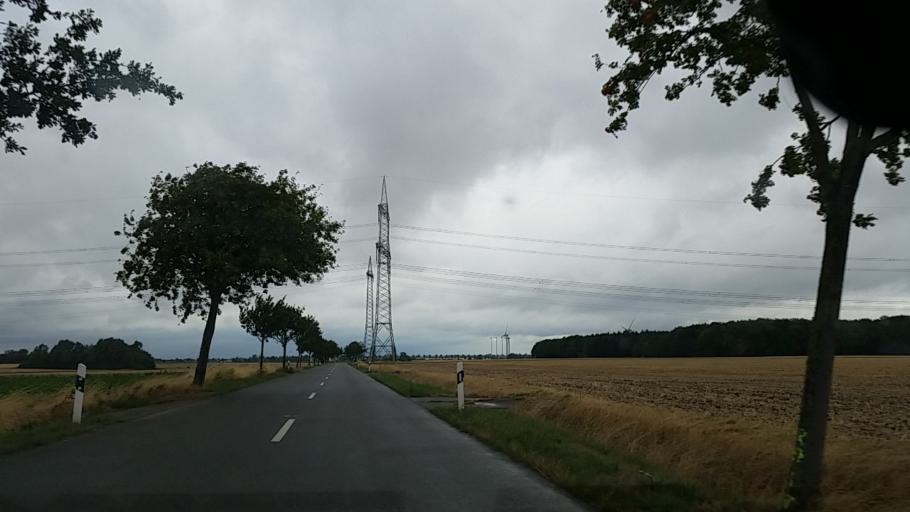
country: DE
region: Lower Saxony
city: Lehre
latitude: 52.3741
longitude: 10.6674
